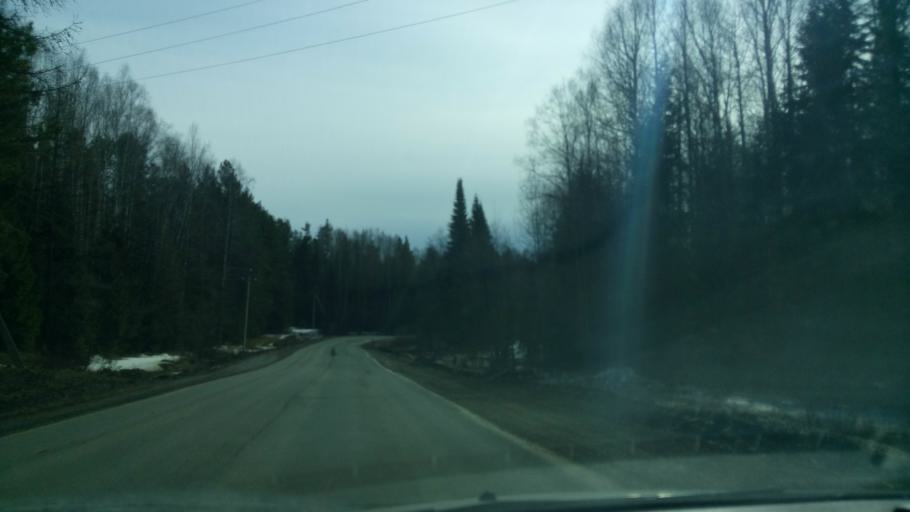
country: RU
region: Sverdlovsk
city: Chernoistochinsk
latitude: 57.7202
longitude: 59.7848
